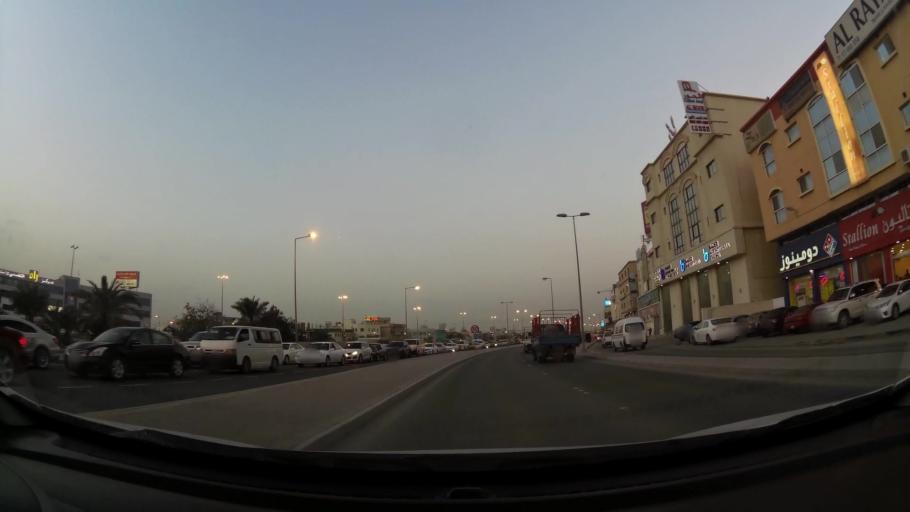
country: BH
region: Manama
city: Jidd Hafs
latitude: 26.2000
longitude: 50.5594
